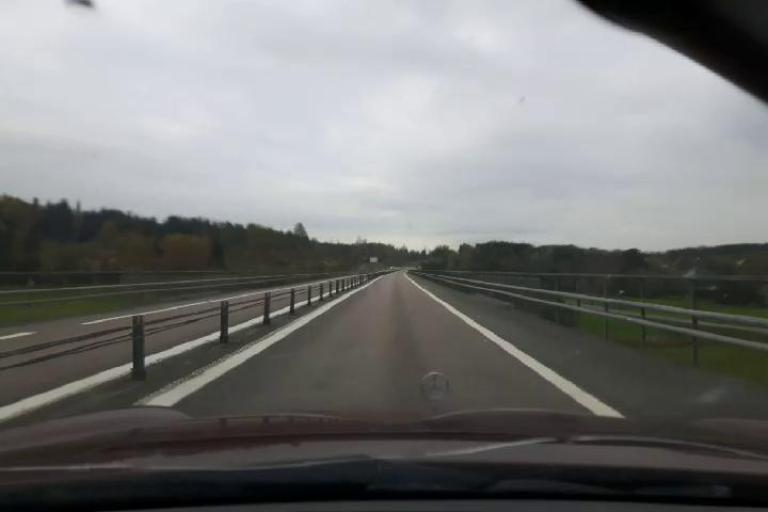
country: SE
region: Vaesternorrland
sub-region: Kramfors Kommun
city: Nordingra
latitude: 62.9217
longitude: 18.0993
